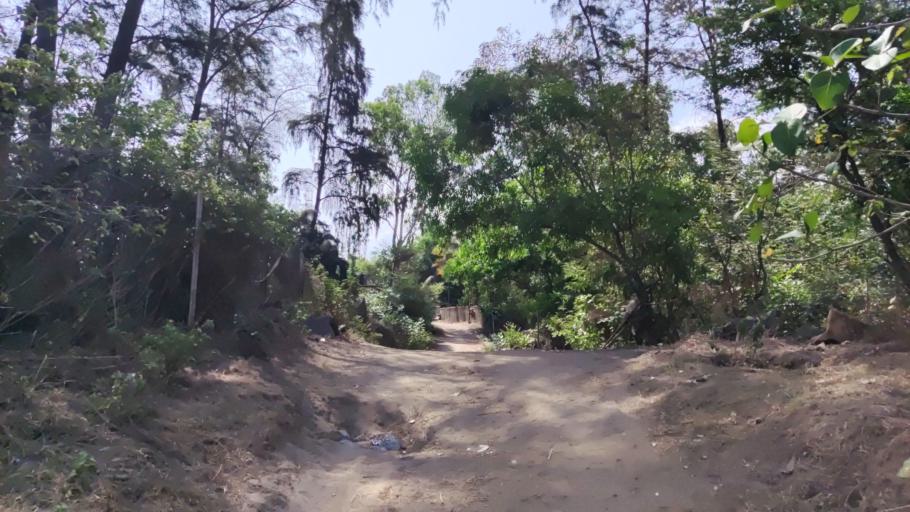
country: IN
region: Daman and Diu
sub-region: Daman District
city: Daman
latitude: 20.3913
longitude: 72.8283
